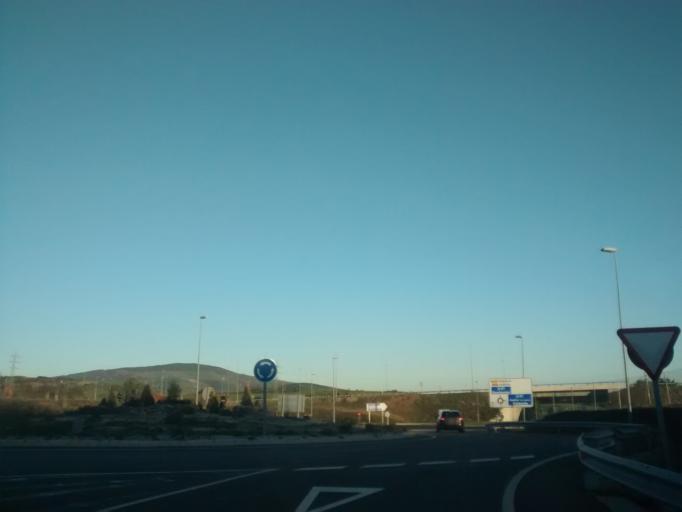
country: ES
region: Cantabria
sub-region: Provincia de Cantabria
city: Reinosa
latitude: 43.0076
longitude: -4.1276
